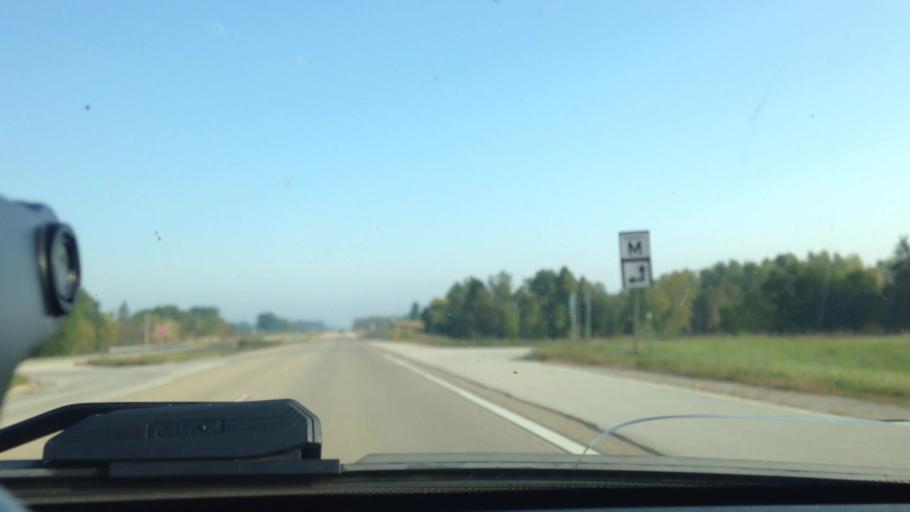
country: US
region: Wisconsin
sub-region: Oconto County
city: Oconto Falls
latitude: 45.0081
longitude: -88.0450
